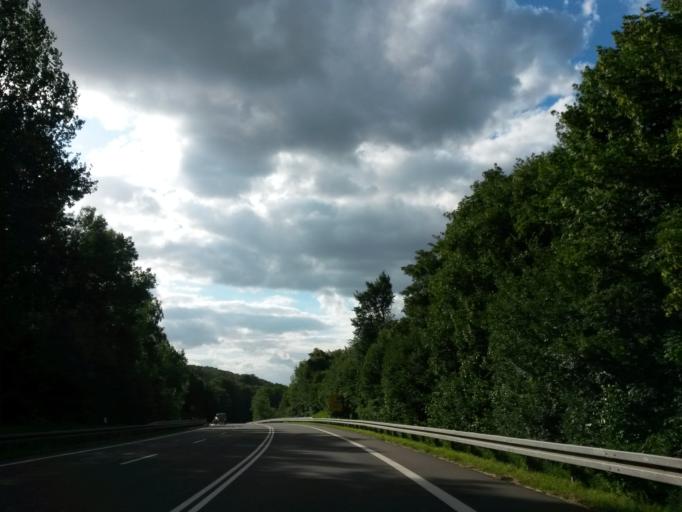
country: DE
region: North Rhine-Westphalia
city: Waldbrol
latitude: 50.9286
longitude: 7.6282
